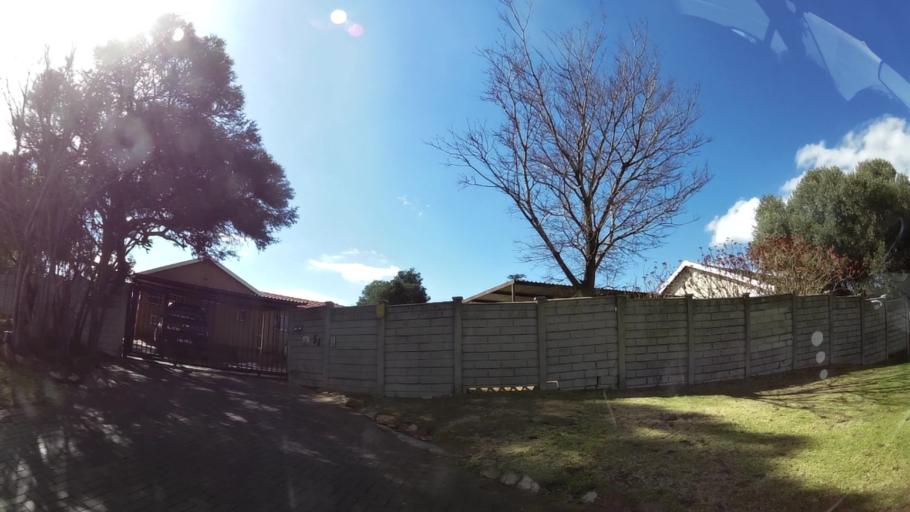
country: ZA
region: Gauteng
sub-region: West Rand District Municipality
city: Krugersdorp
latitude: -26.1025
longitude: 27.7943
